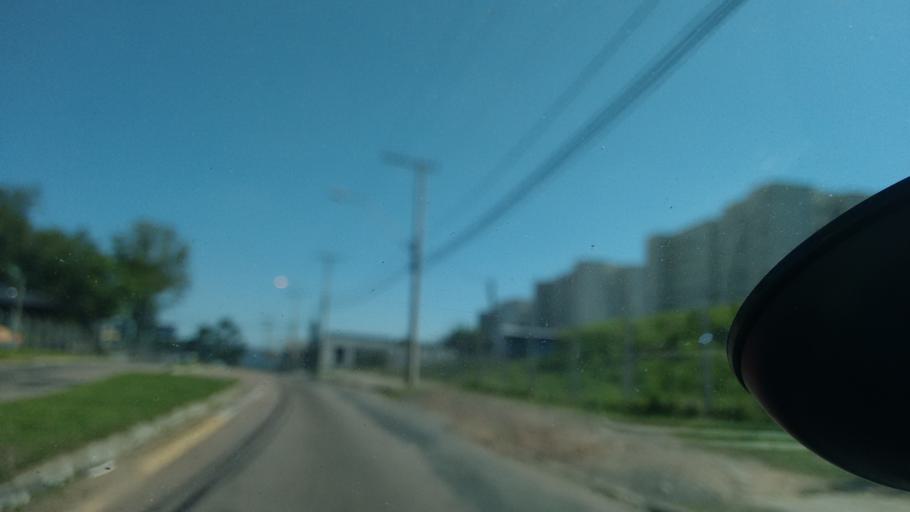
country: BR
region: Rio Grande do Sul
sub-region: Cachoeirinha
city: Cachoeirinha
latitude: -30.0046
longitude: -51.1277
